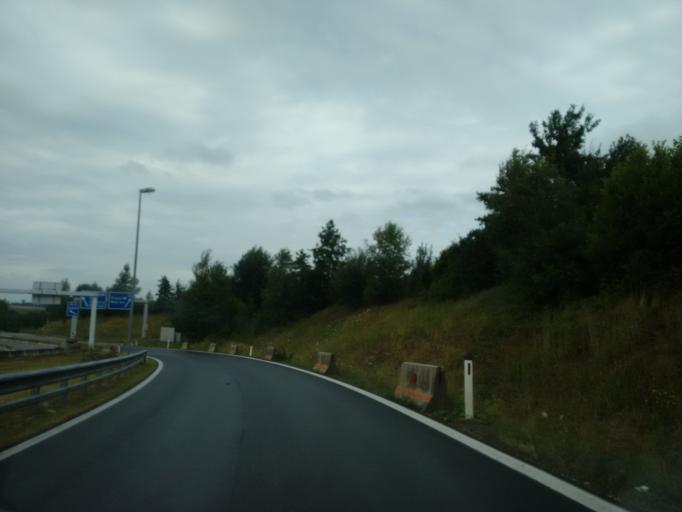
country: AT
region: Upper Austria
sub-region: Wels-Land
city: Sattledt
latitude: 48.0679
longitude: 14.0331
